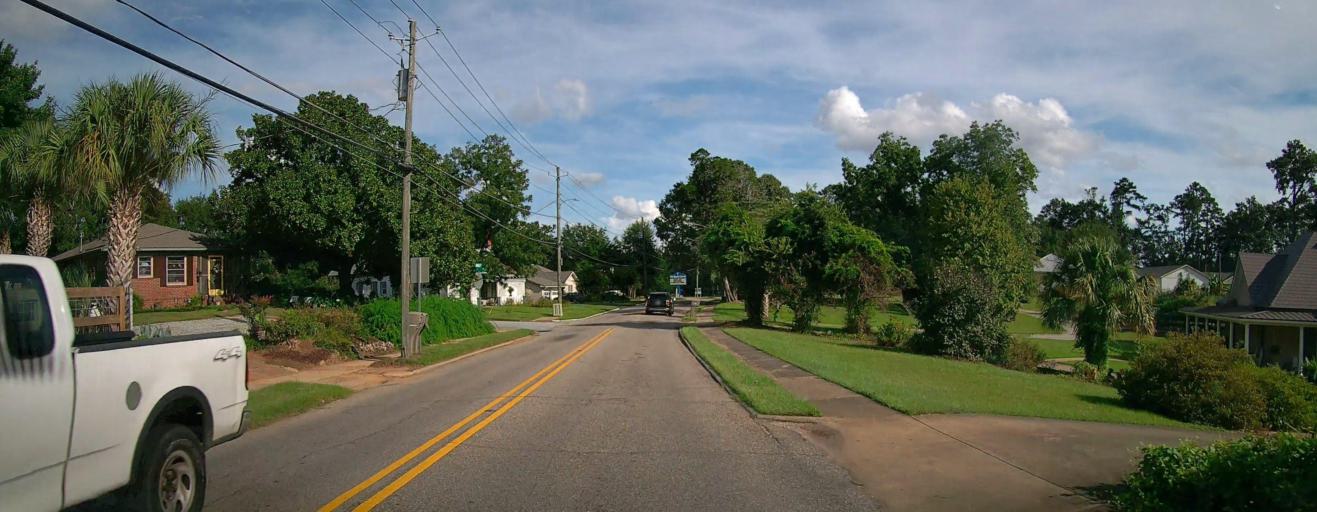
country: US
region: Alabama
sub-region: Russell County
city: Phenix City
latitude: 32.4877
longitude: -85.0096
